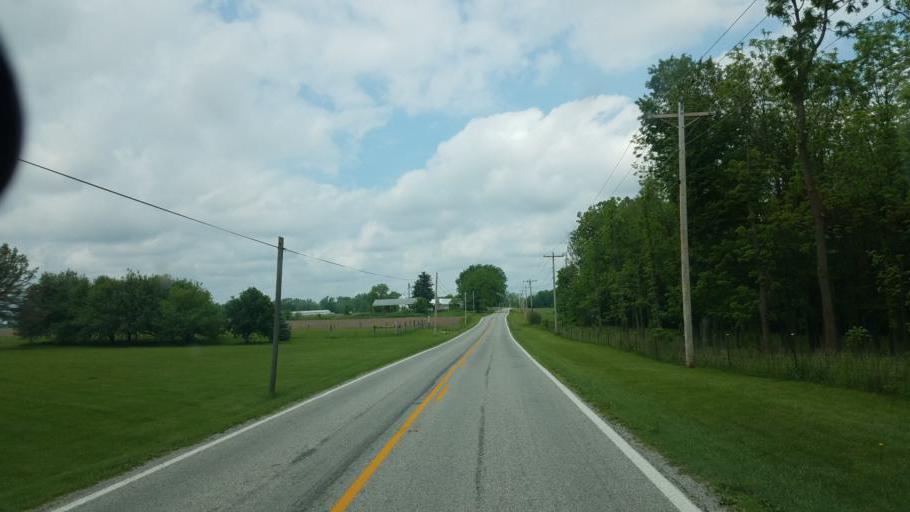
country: US
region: Ohio
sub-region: Marion County
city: Prospect
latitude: 40.4060
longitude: -83.1978
